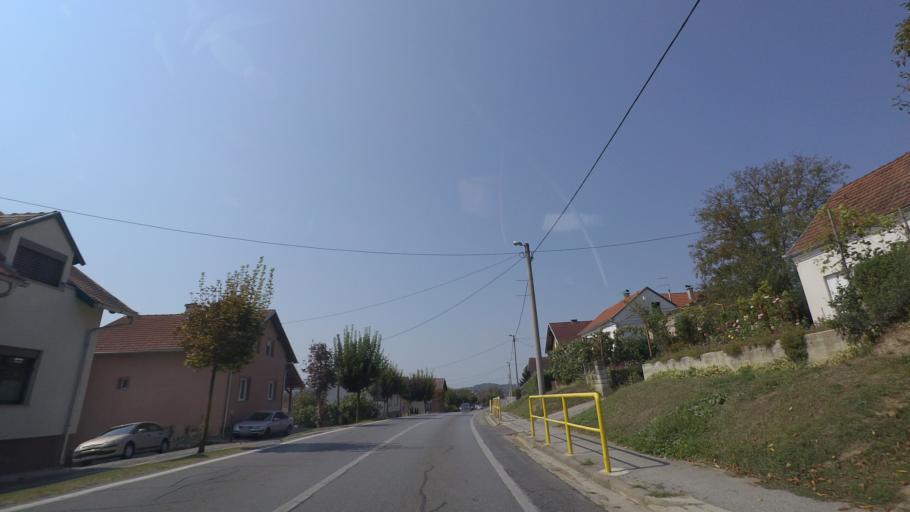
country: HR
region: Pozesko-Slavonska
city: Lipik
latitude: 45.4186
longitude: 17.1723
